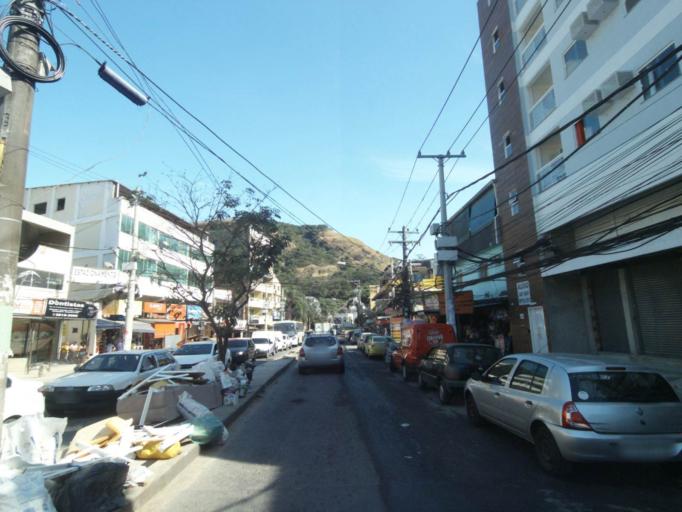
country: BR
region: Rio de Janeiro
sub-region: Rio De Janeiro
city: Rio de Janeiro
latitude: -22.9876
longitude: -43.3093
